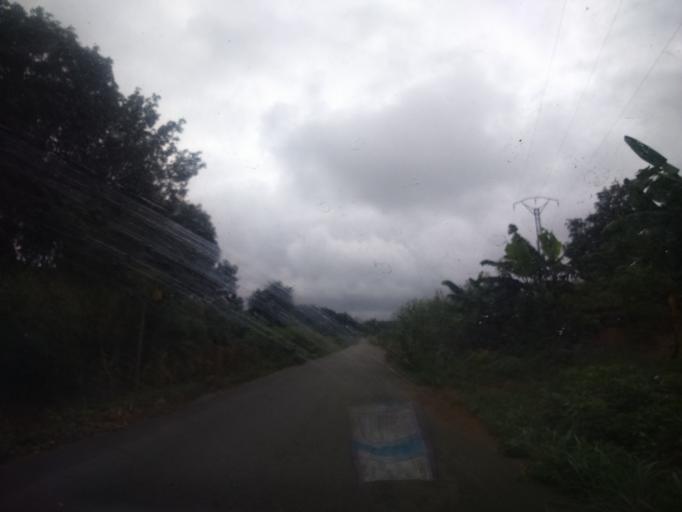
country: CI
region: Sud-Comoe
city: Bonoua
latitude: 5.2827
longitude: -3.4760
